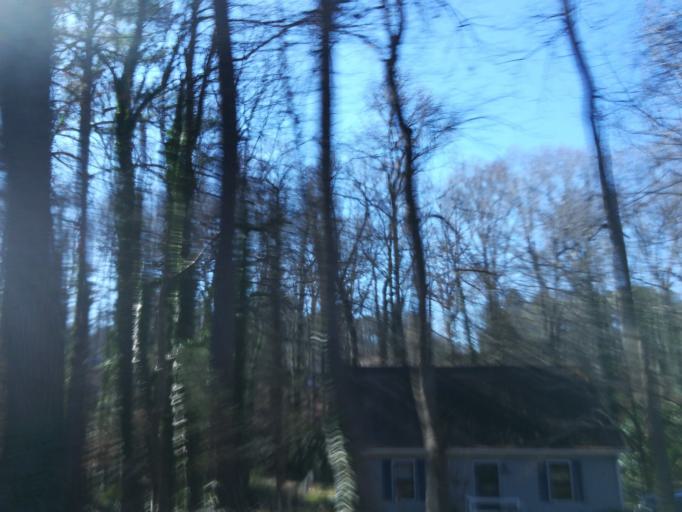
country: US
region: North Carolina
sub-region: Durham County
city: Durham
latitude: 36.0462
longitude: -78.9682
